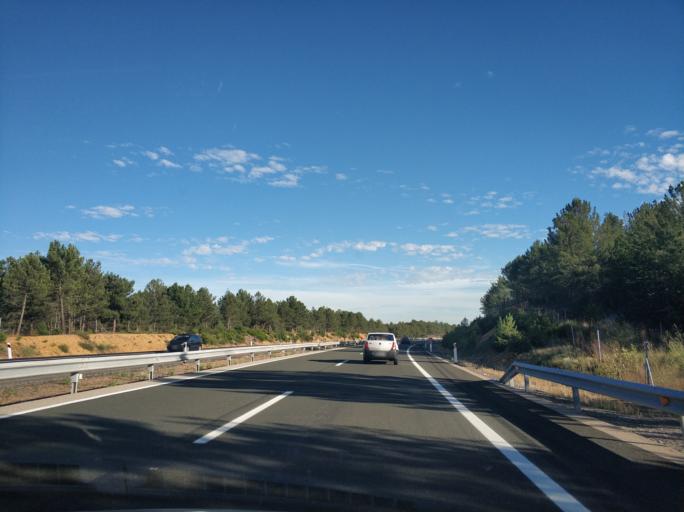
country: ES
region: Castille and Leon
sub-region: Provincia de Leon
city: Cimanes del Tejar
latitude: 42.6444
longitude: -5.7458
